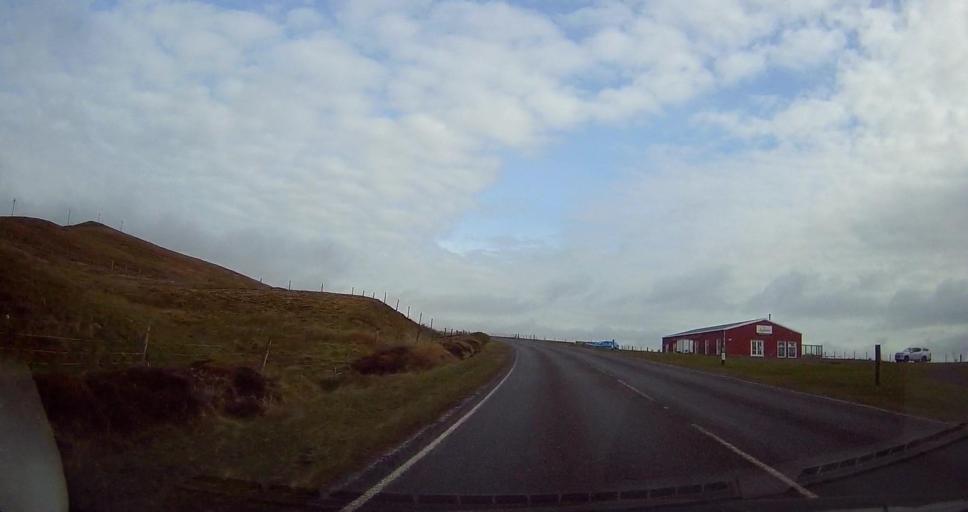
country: GB
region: Scotland
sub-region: Shetland Islands
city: Sandwick
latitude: 60.0616
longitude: -1.2216
